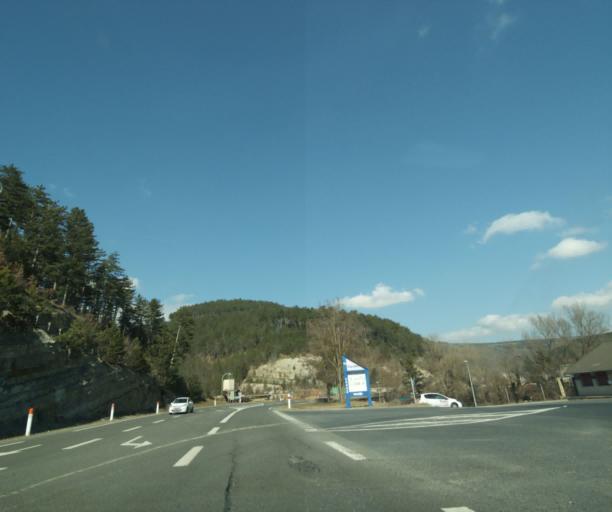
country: FR
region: Languedoc-Roussillon
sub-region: Departement de la Lozere
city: Mende
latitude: 44.5262
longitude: 3.5216
